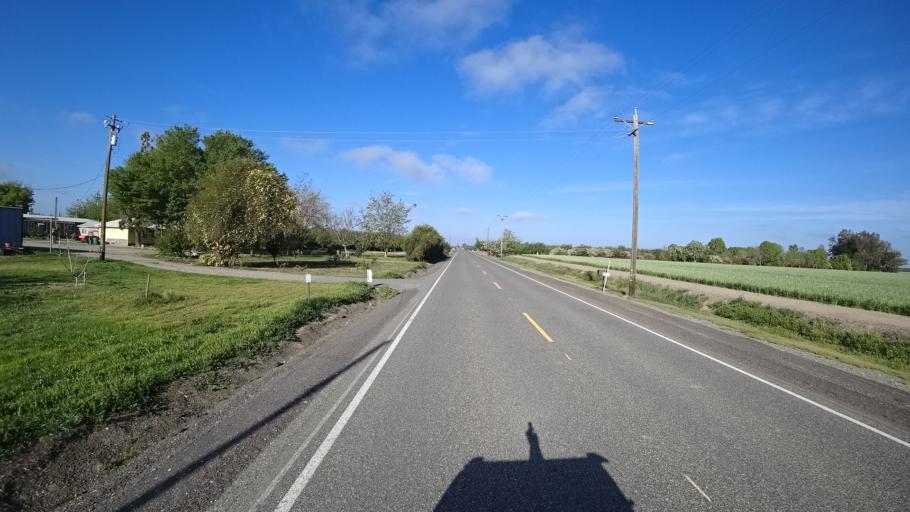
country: US
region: California
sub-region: Glenn County
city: Willows
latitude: 39.5822
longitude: -122.1429
